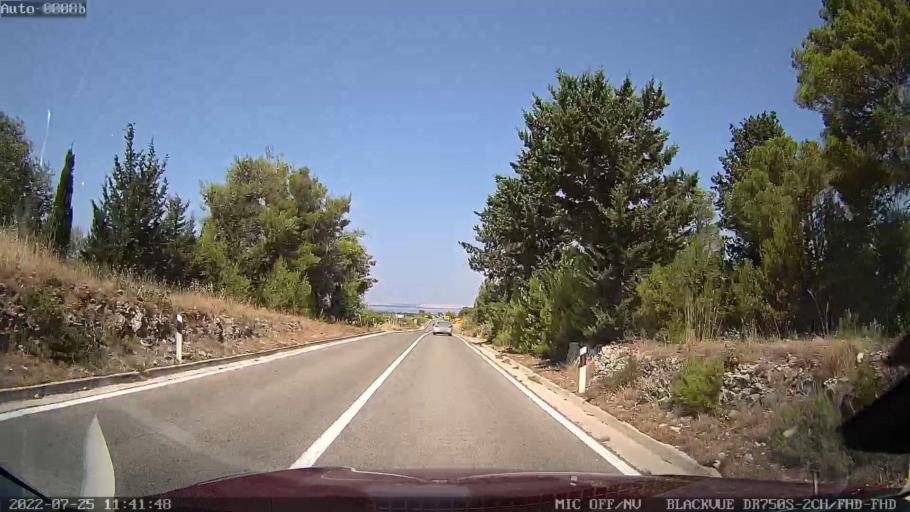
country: HR
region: Zadarska
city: Razanac
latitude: 44.2700
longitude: 15.3435
